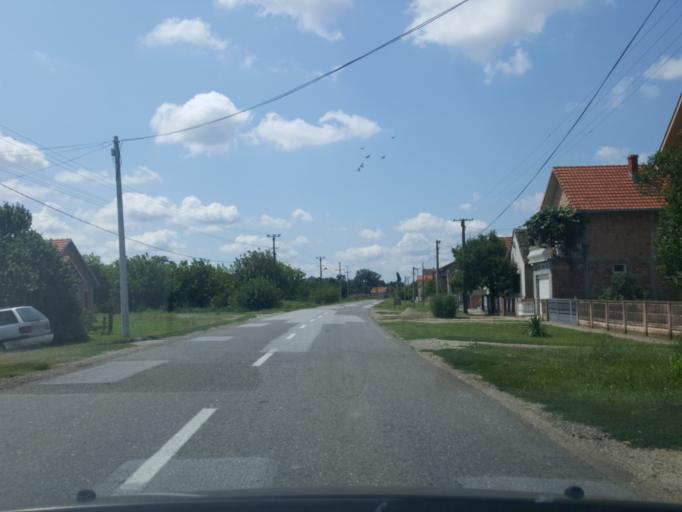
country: RS
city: Salas Nocajski
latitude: 44.9323
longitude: 19.5675
